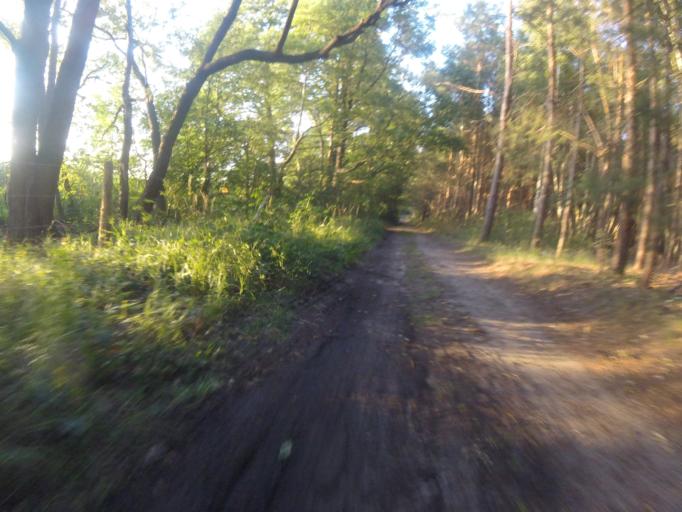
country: DE
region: Brandenburg
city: Gross Koris
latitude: 52.1763
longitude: 13.7003
